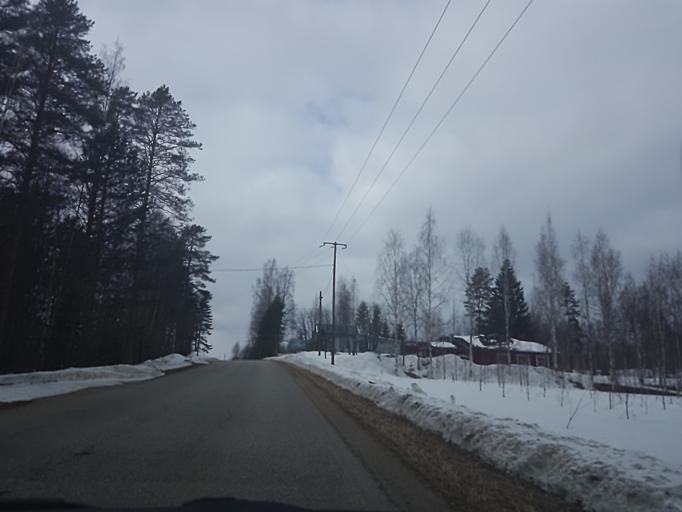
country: FI
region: Northern Savo
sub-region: Koillis-Savo
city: Kaavi
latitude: 63.0001
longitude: 28.6920
